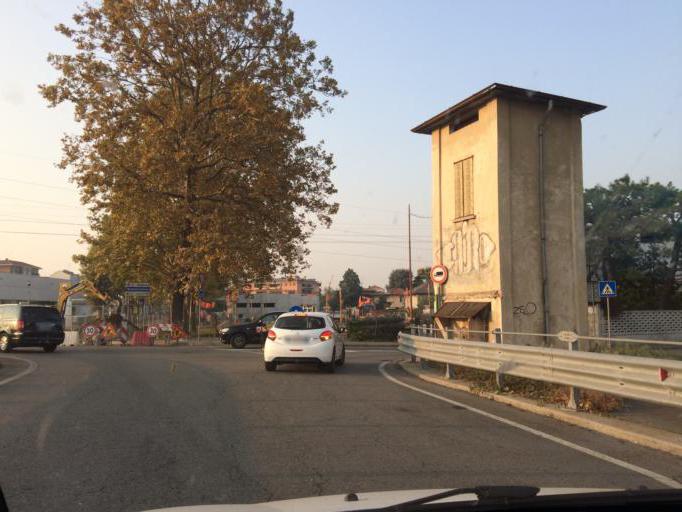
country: IT
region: Lombardy
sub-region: Provincia di Varese
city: Castellanza
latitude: 45.6126
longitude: 8.8871
